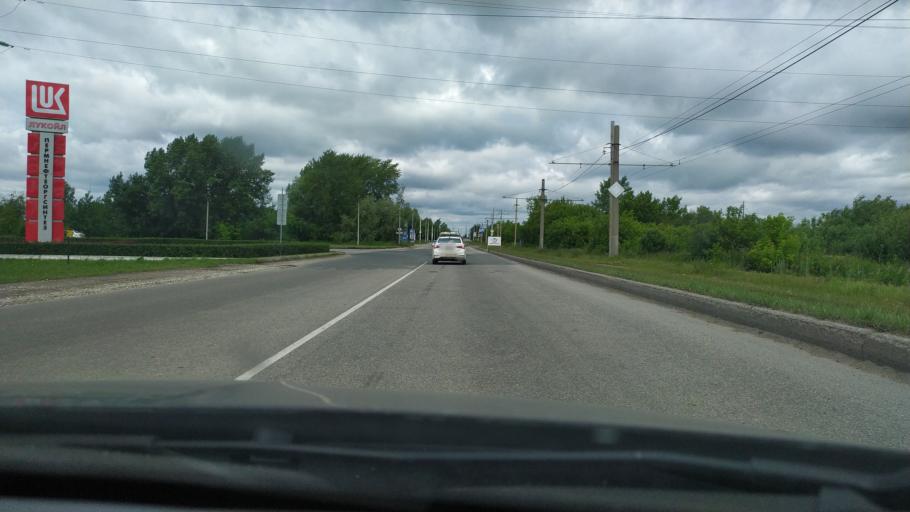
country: RU
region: Perm
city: Kondratovo
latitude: 57.9315
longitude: 56.1270
